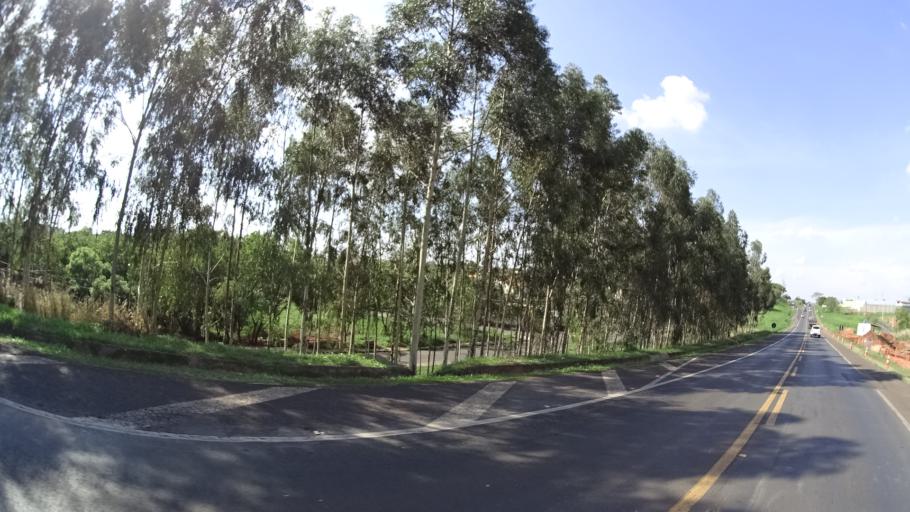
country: BR
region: Sao Paulo
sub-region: Sao Jose Do Rio Preto
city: Sao Jose do Rio Preto
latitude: -20.8481
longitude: -49.3755
